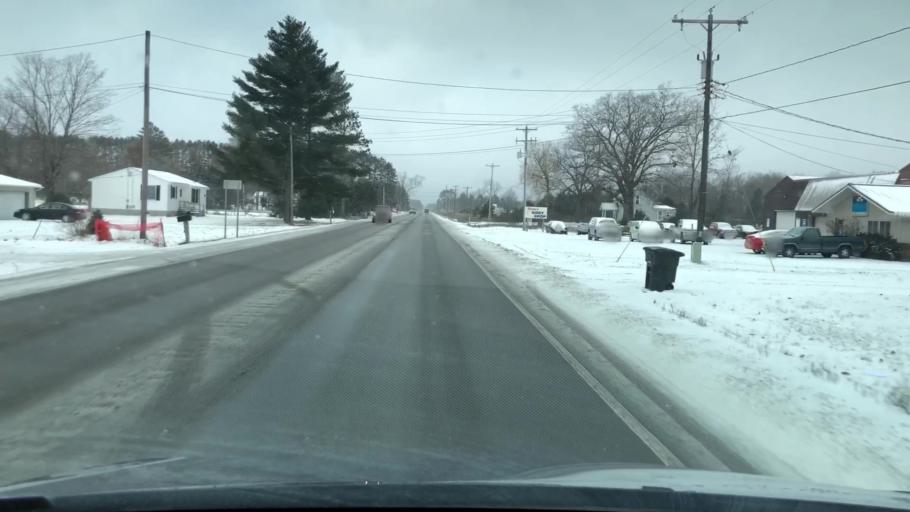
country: US
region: Michigan
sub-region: Wexford County
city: Cadillac
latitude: 44.2813
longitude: -85.4381
